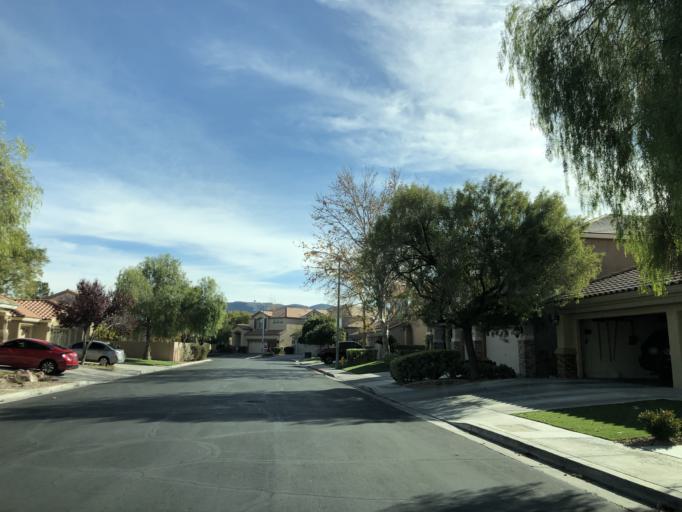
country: US
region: Nevada
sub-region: Clark County
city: Whitney
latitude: 36.0154
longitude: -115.0791
